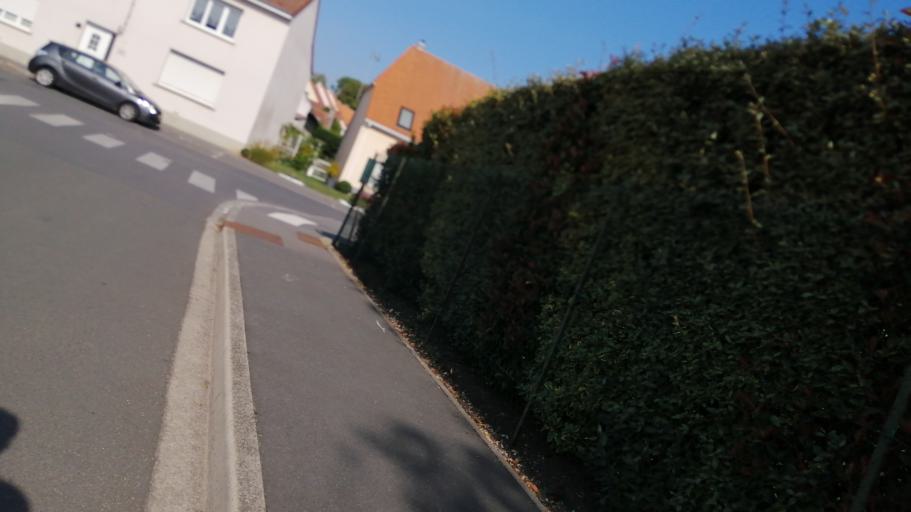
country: FR
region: Nord-Pas-de-Calais
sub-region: Departement du Pas-de-Calais
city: Dainville
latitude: 50.2806
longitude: 2.7262
